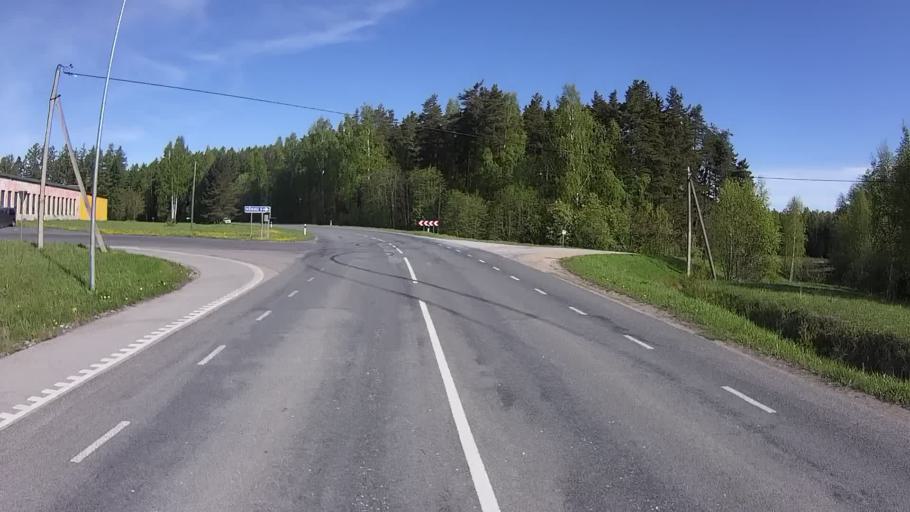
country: EE
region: Polvamaa
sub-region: Polva linn
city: Polva
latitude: 58.2171
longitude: 27.0687
